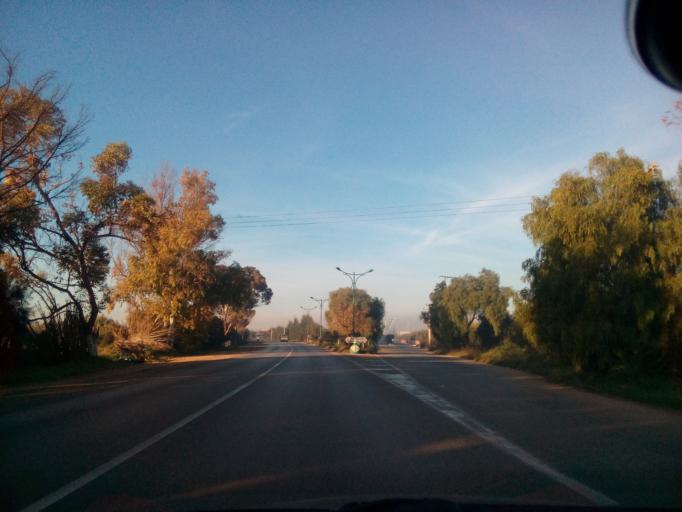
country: DZ
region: Relizane
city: Relizane
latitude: 35.7242
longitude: 0.3699
